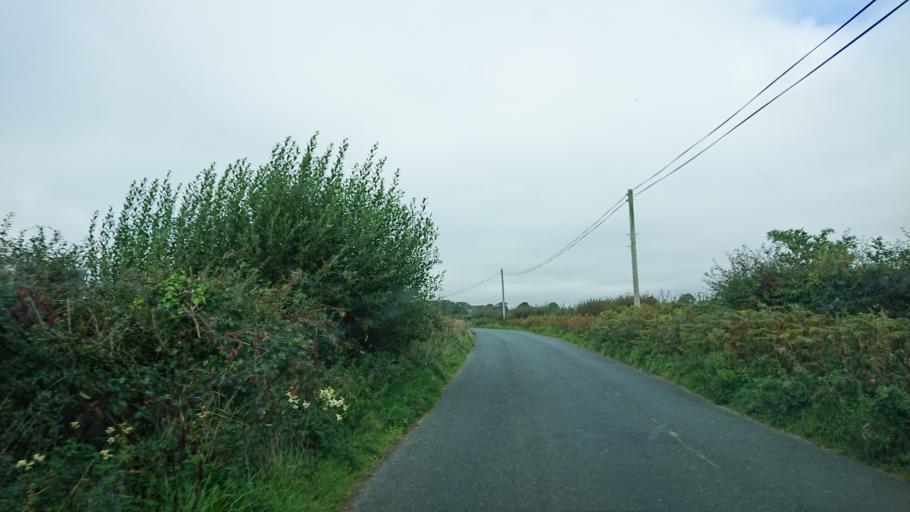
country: IE
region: Munster
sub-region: Waterford
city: Tra Mhor
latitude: 52.1882
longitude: -7.1166
